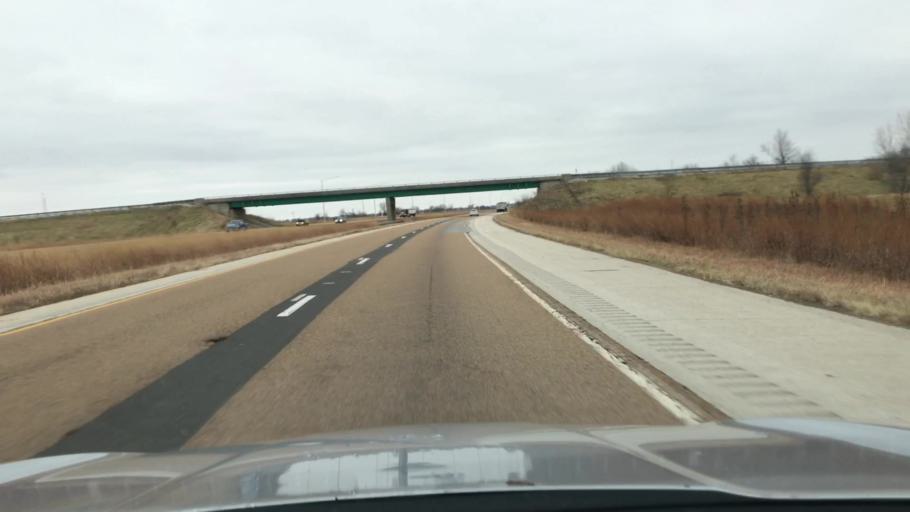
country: US
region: Illinois
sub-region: Montgomery County
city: Litchfield
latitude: 39.2355
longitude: -89.6415
